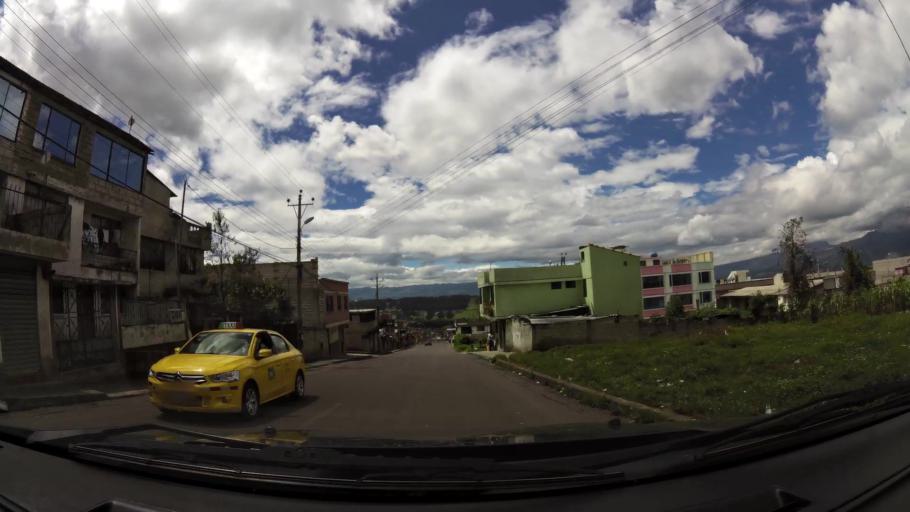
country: EC
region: Pichincha
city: Sangolqui
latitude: -0.3436
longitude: -78.5610
